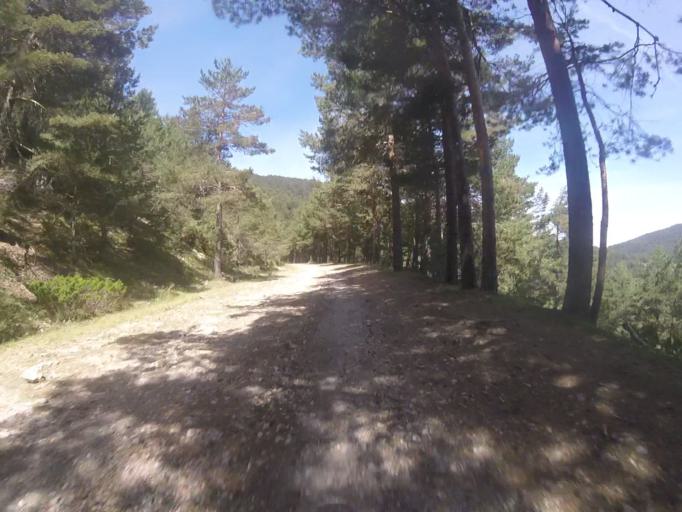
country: ES
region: Madrid
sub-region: Provincia de Madrid
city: Cercedilla
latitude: 40.8069
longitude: -4.0520
